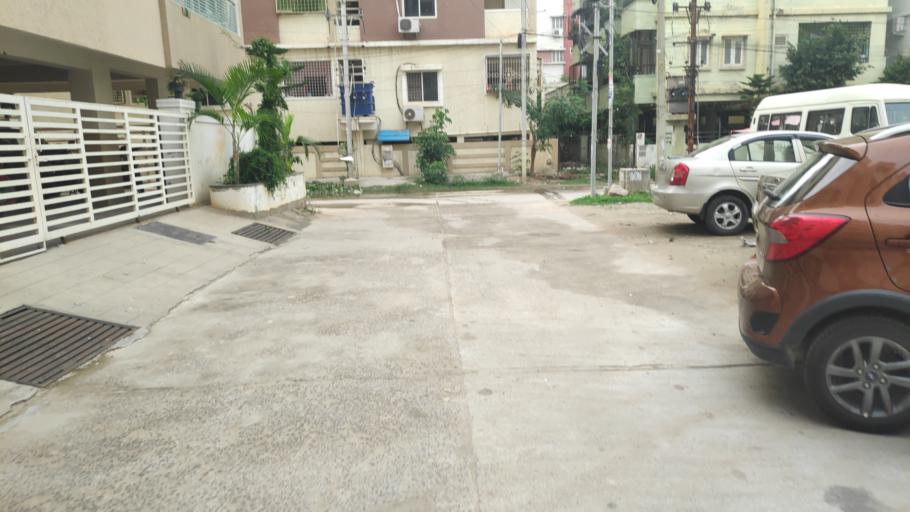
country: IN
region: Telangana
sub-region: Rangareddi
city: Kukatpalli
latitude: 17.5144
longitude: 78.3889
